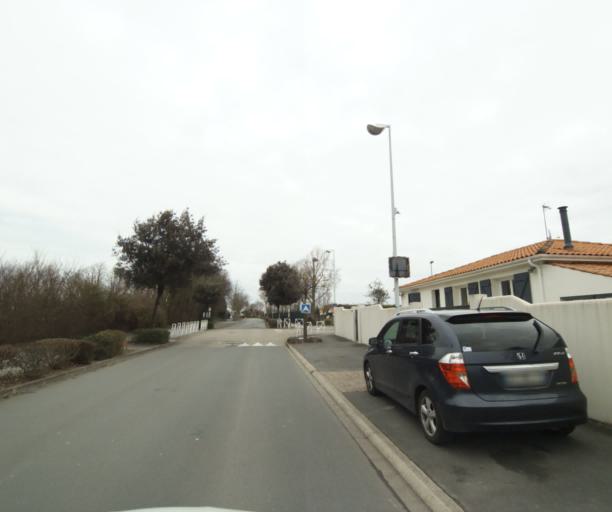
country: FR
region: Poitou-Charentes
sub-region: Departement de la Charente-Maritime
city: Lagord
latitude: 46.1900
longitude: -1.1578
